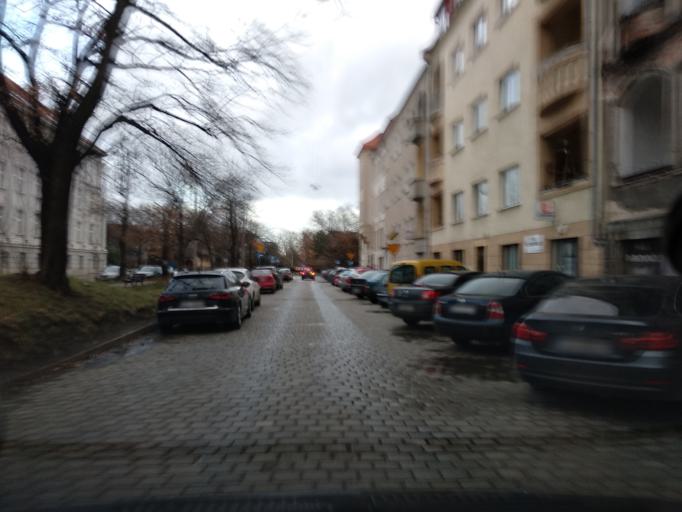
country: PL
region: Lower Silesian Voivodeship
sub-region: Powiat wroclawski
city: Wroclaw
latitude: 51.0885
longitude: 17.0170
